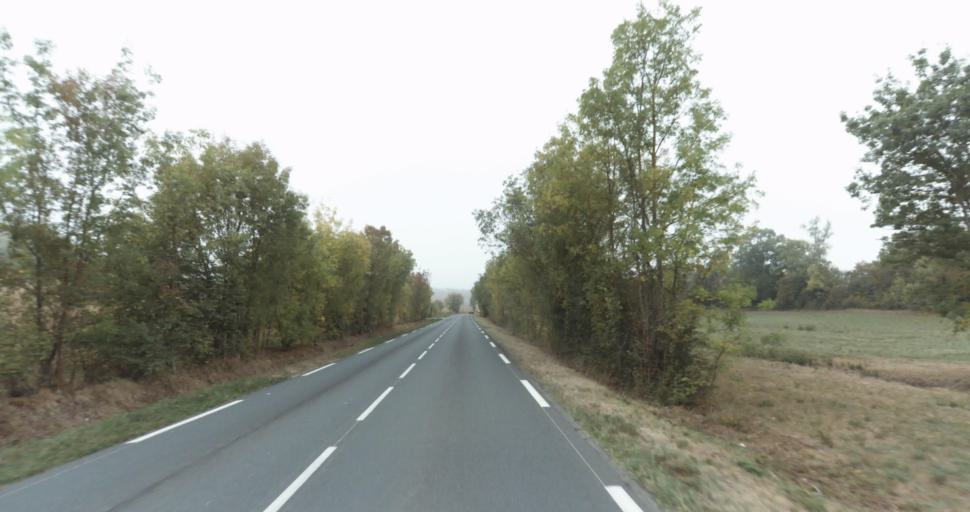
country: FR
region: Midi-Pyrenees
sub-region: Departement du Gers
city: Preignan
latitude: 43.6807
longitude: 0.6190
